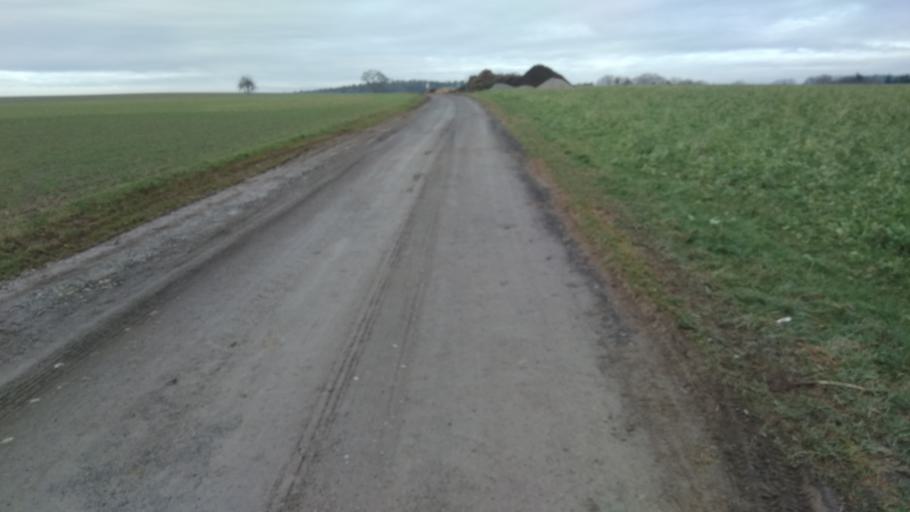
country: DE
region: Baden-Wuerttemberg
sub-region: Karlsruhe Region
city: Mosbach
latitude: 49.3547
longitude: 9.1765
